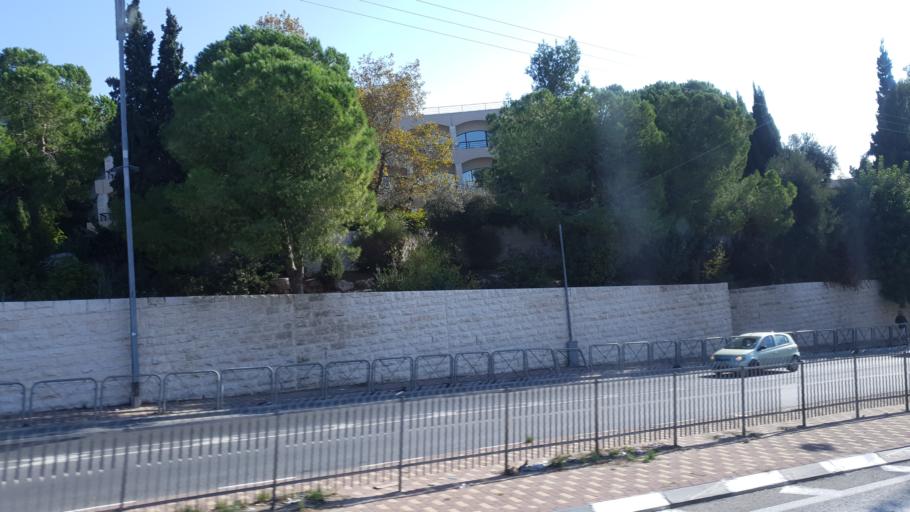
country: PS
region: West Bank
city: East Jerusalem
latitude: 31.7979
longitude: 35.2345
